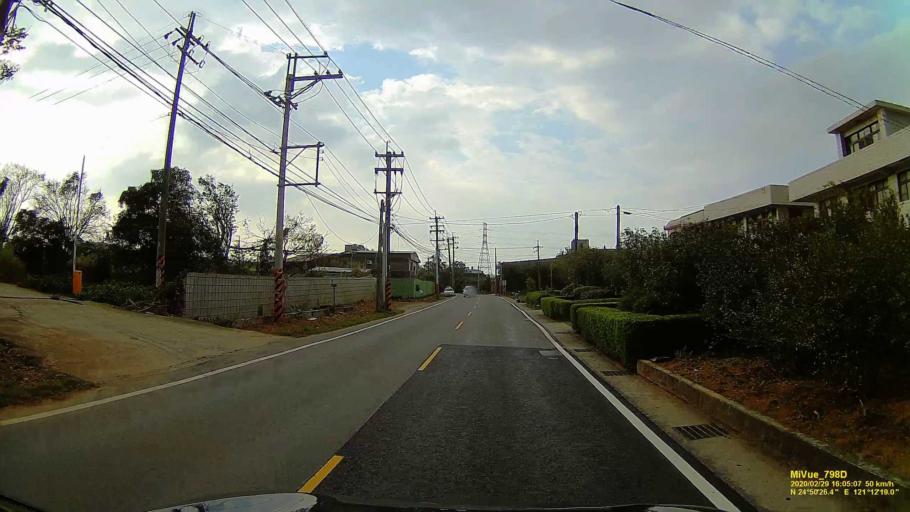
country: TW
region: Taiwan
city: Daxi
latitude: 24.8408
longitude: 121.2050
